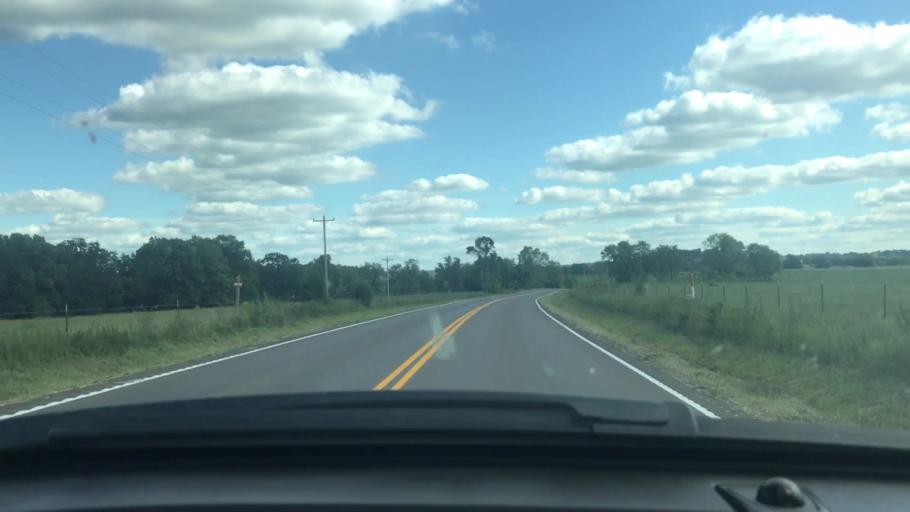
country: US
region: Missouri
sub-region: Wright County
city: Mountain Grove
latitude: 37.2963
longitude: -92.3098
